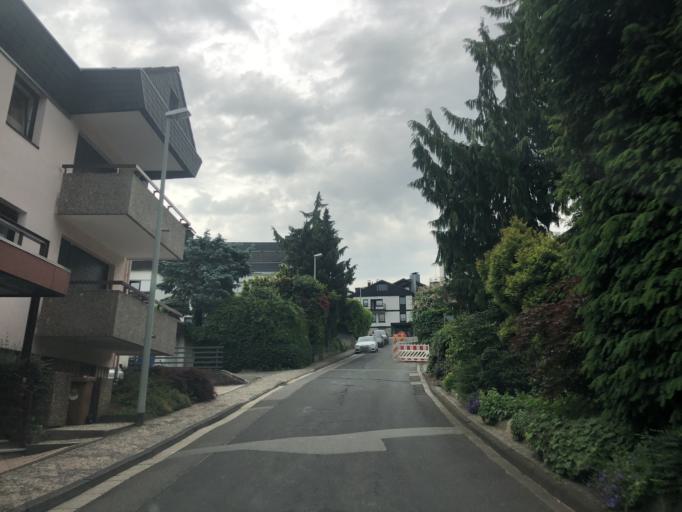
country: DE
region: Hesse
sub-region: Regierungsbezirk Darmstadt
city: Konigstein im Taunus
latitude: 50.1749
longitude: 8.4660
